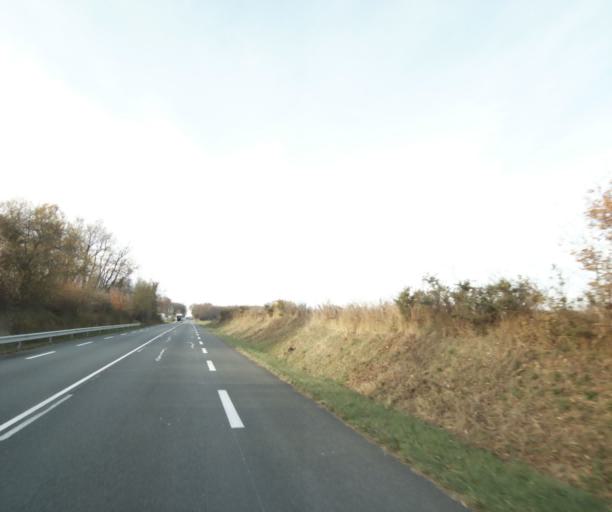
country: FR
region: Poitou-Charentes
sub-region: Departement de la Charente-Maritime
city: Chaniers
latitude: 45.7422
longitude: -0.5517
